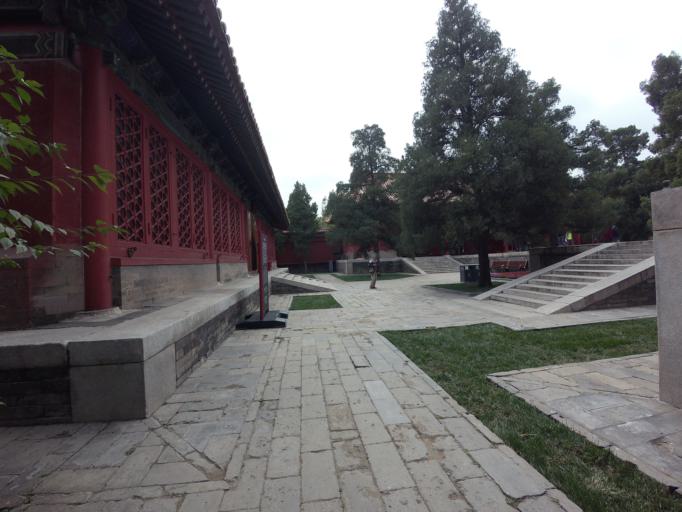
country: CN
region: Beijing
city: Beijing
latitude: 39.9142
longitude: 116.3934
